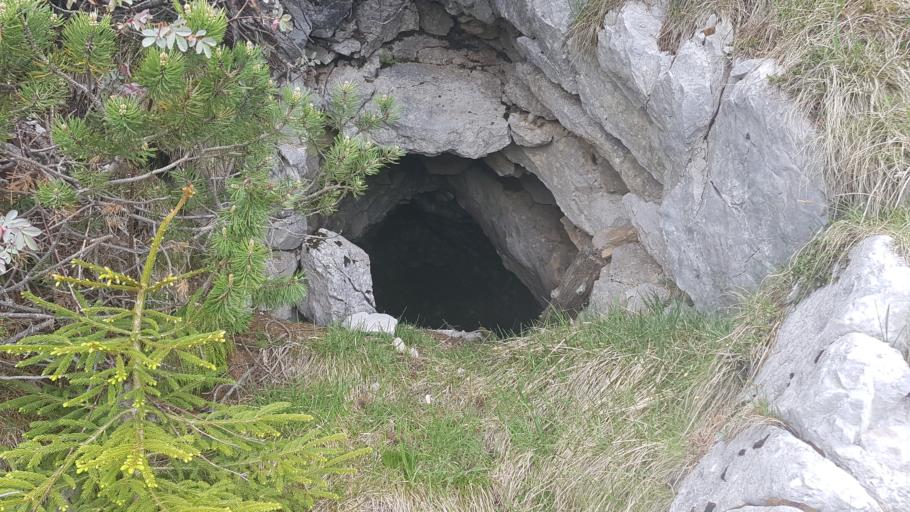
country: IT
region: Friuli Venezia Giulia
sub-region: Provincia di Udine
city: Paularo
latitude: 46.5358
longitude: 13.1835
